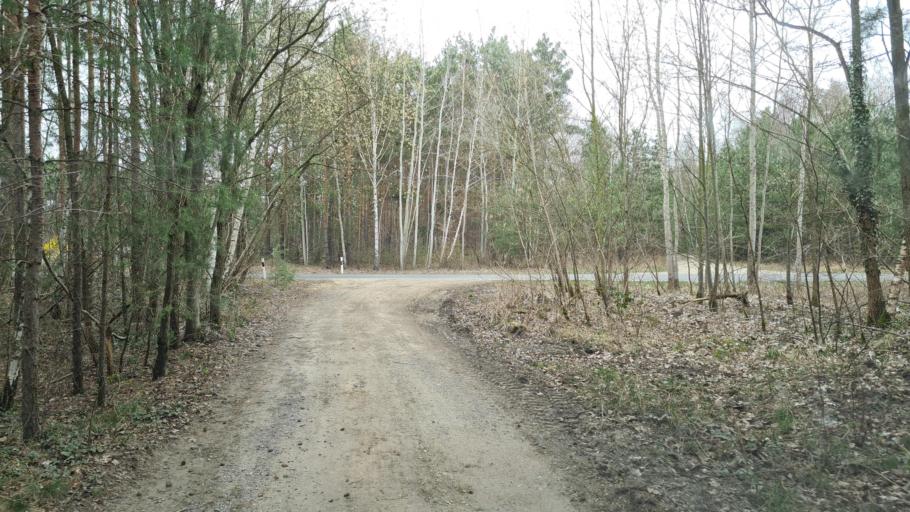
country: DE
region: Brandenburg
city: Lauchhammer
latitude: 51.5114
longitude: 13.7251
